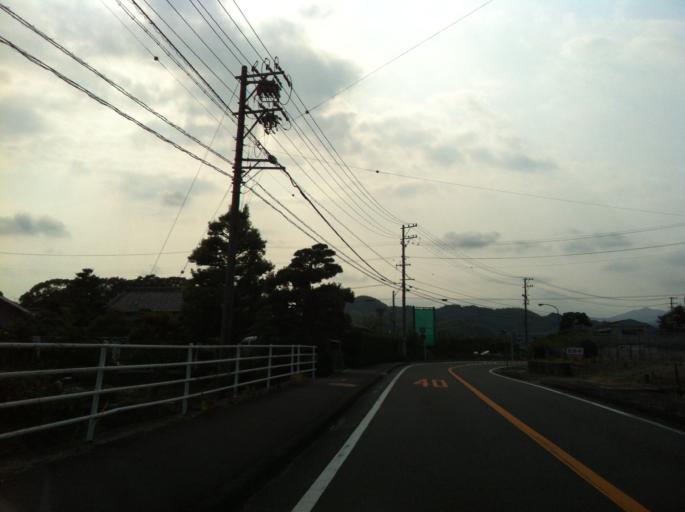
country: JP
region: Shizuoka
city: Fujieda
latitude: 34.9101
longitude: 138.2725
